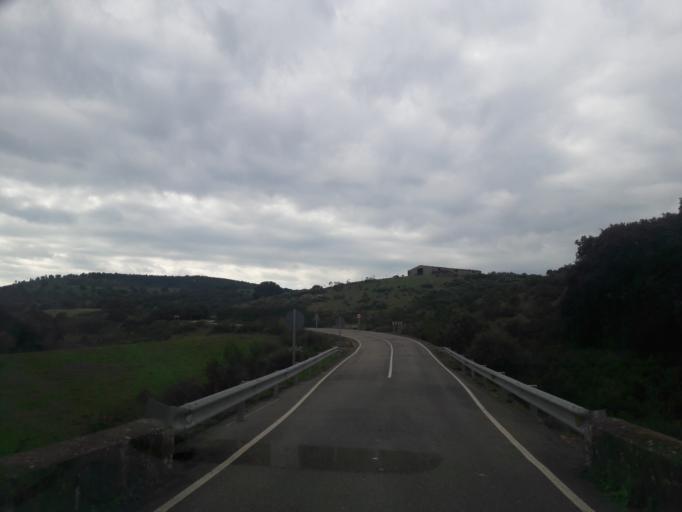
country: ES
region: Castille and Leon
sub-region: Provincia de Salamanca
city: Serradilla del Arroyo
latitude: 40.5253
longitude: -6.4037
